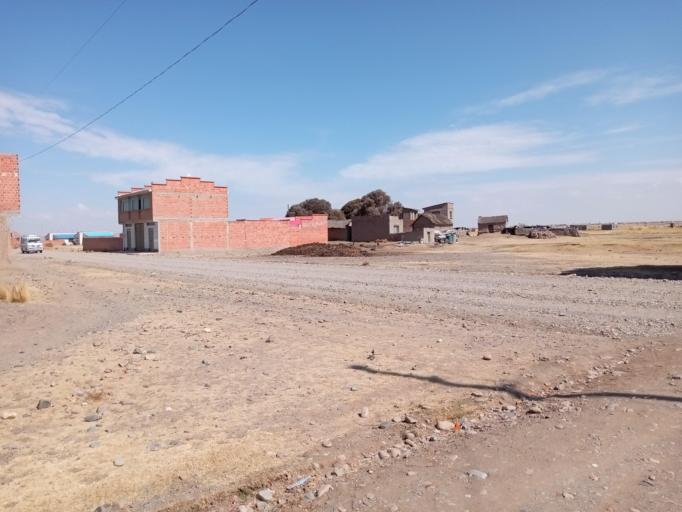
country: BO
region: La Paz
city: Batallas
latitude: -16.4387
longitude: -68.3750
